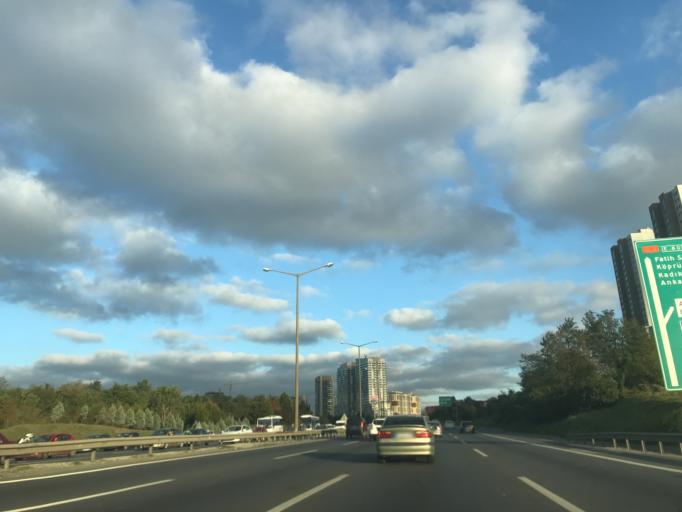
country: TR
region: Istanbul
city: Sisli
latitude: 41.0926
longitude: 28.9358
